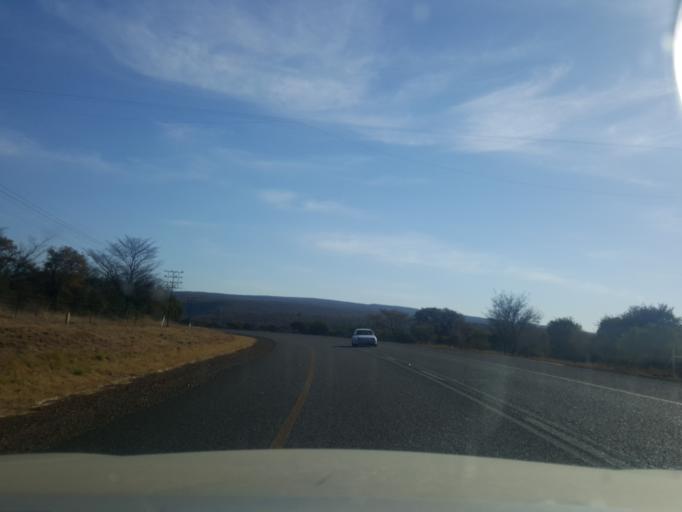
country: ZA
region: North-West
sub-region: Ngaka Modiri Molema District Municipality
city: Zeerust
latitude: -25.5177
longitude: 26.1663
